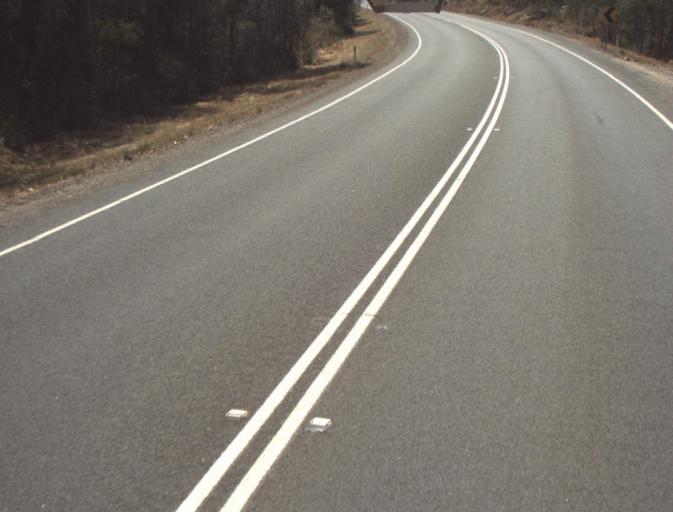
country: AU
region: Tasmania
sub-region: Launceston
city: Mayfield
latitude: -41.3536
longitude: 147.1438
